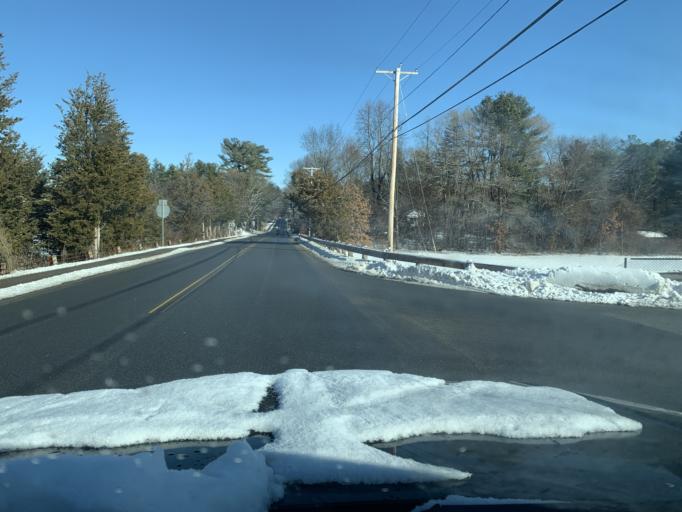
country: US
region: Massachusetts
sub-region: Essex County
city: Topsfield
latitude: 42.6290
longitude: -70.9752
